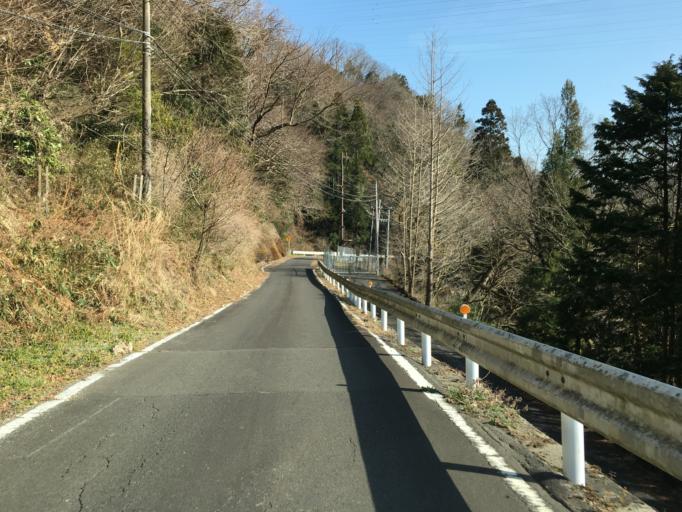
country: JP
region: Ibaraki
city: Kitaibaraki
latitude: 36.7778
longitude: 140.6802
